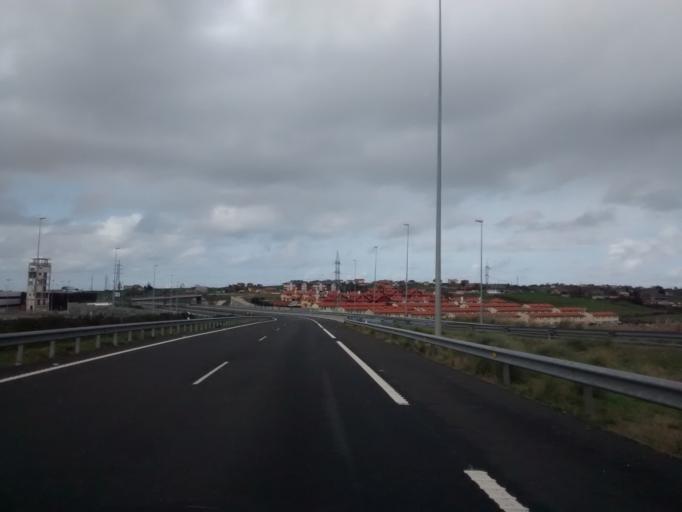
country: ES
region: Cantabria
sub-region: Provincia de Cantabria
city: Santa Cruz de Bezana
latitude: 43.4385
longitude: -3.8758
